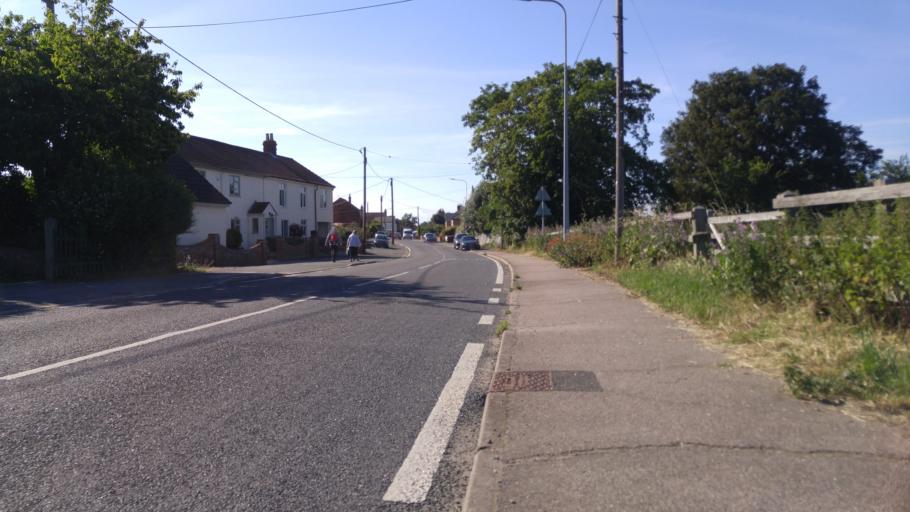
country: GB
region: England
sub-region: Essex
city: Rowhedge
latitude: 51.8647
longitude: 0.9328
